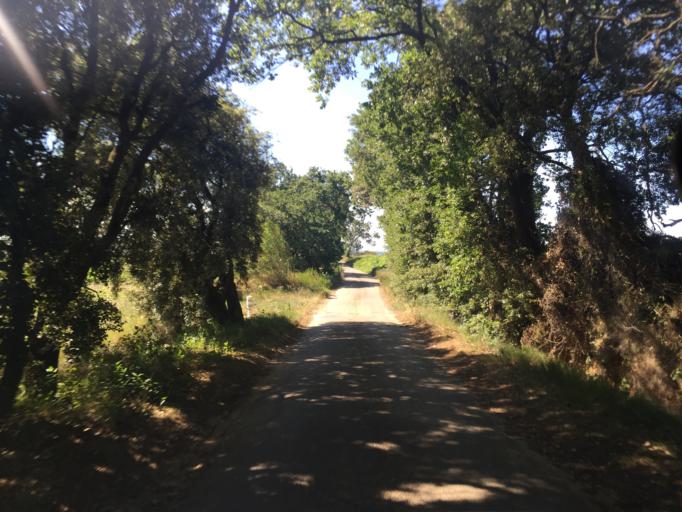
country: FR
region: Provence-Alpes-Cote d'Azur
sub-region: Departement du Vaucluse
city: Chateauneuf-du-Pape
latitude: 44.0850
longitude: 4.8061
